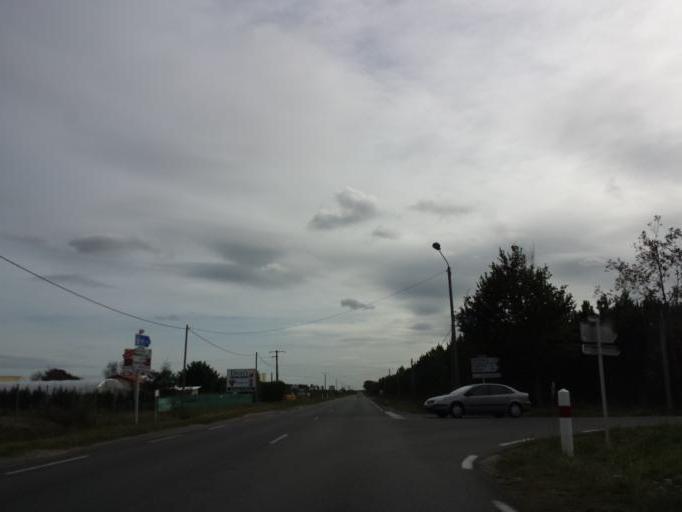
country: FR
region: Aquitaine
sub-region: Departement de la Gironde
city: Marcheprime
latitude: 44.7714
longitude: -0.9269
